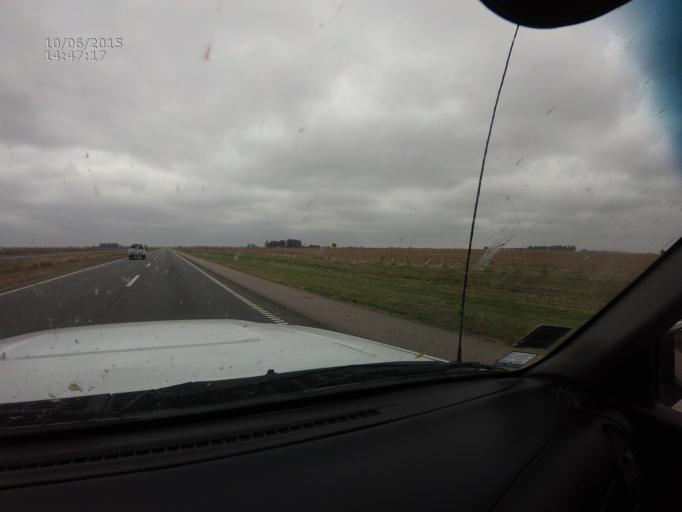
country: AR
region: Cordoba
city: Oliva
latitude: -31.9605
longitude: -63.5897
